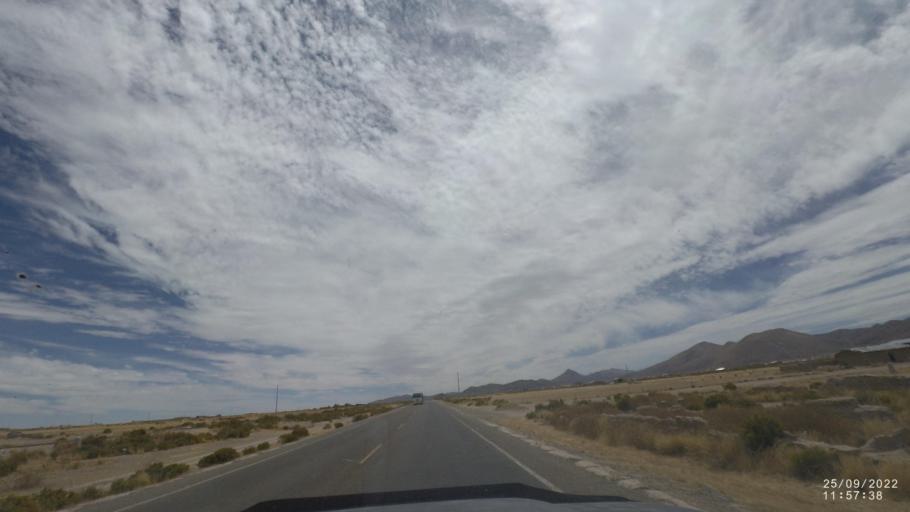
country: BO
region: Oruro
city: Challapata
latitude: -18.8192
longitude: -66.8296
